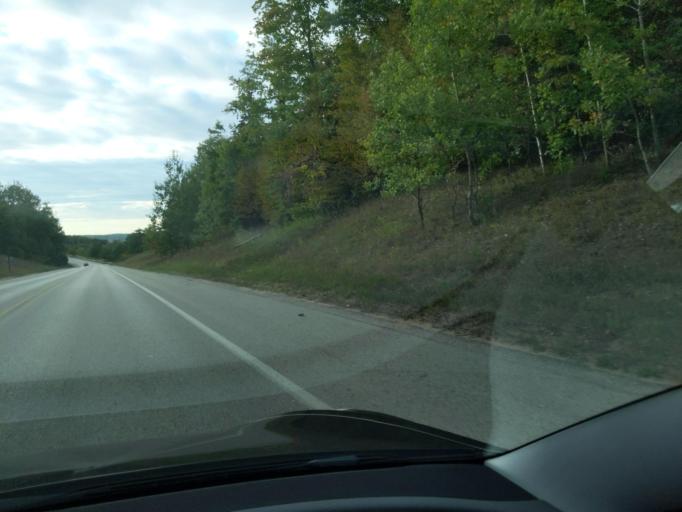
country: US
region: Michigan
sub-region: Kalkaska County
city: Rapid City
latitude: 44.7809
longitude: -85.2804
